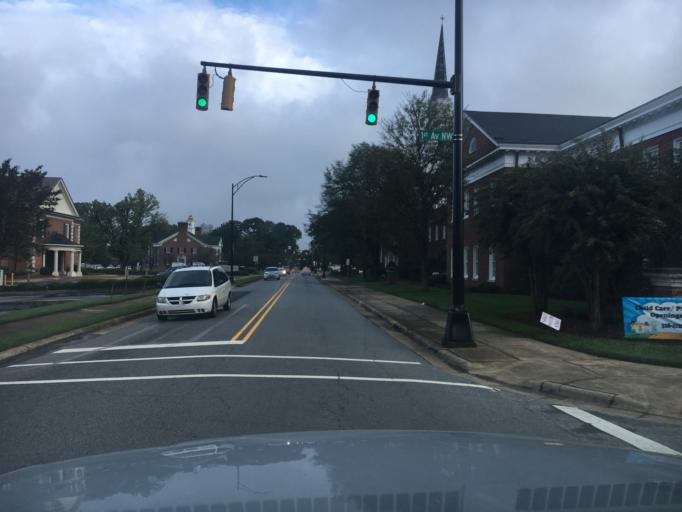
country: US
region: North Carolina
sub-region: Catawba County
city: Hickory
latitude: 35.7331
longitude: -81.3445
